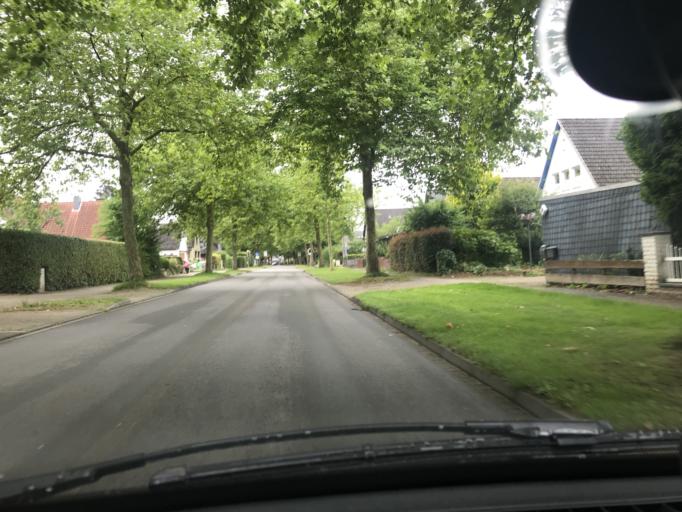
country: DE
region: Schleswig-Holstein
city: Grosshansdorf
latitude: 53.6475
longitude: 10.2804
